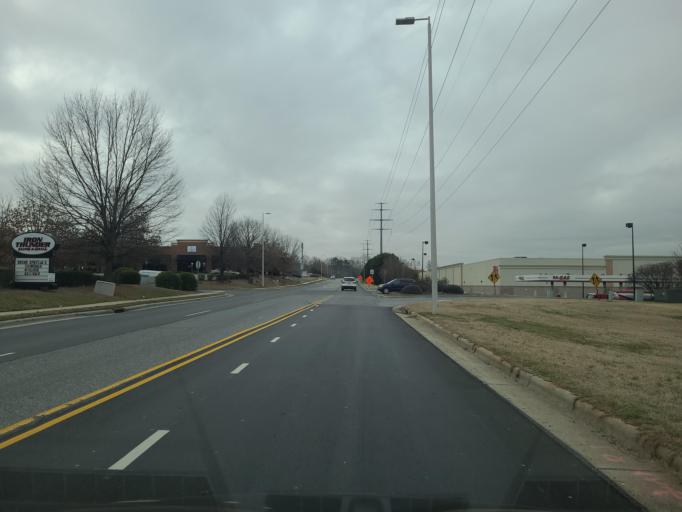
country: US
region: North Carolina
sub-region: Cabarrus County
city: Harrisburg
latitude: 35.3650
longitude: -80.7117
